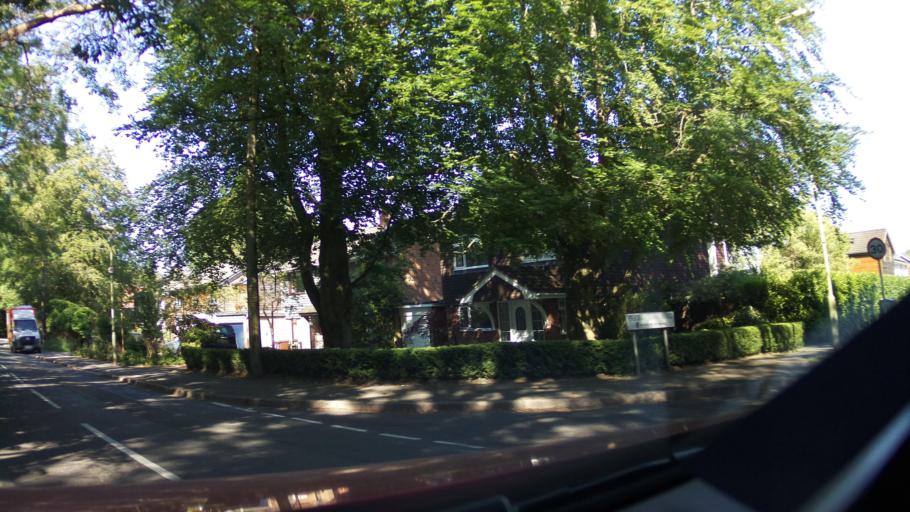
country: GB
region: England
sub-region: Hampshire
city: Winchester
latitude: 51.0855
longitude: -1.3370
